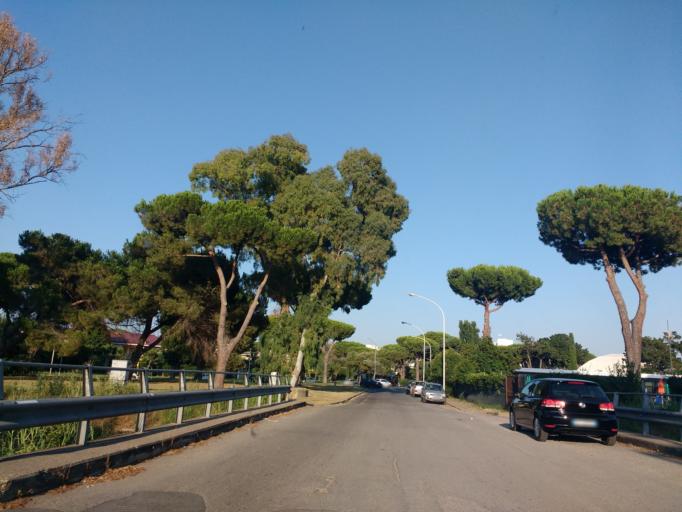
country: IT
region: Latium
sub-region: Citta metropolitana di Roma Capitale
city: Acilia-Castel Fusano-Ostia Antica
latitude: 41.7518
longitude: 12.3494
